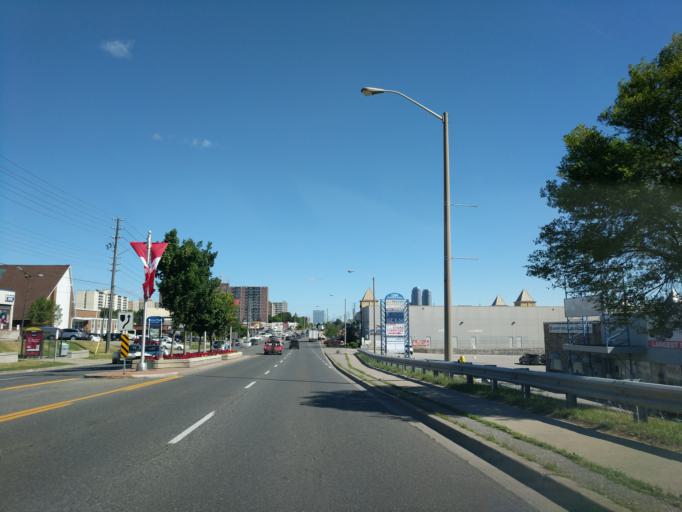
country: CA
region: Ontario
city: Scarborough
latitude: 43.7636
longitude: -79.2802
